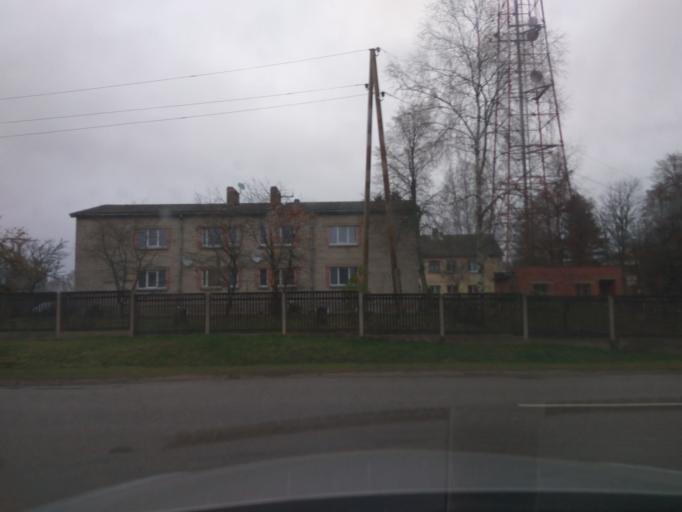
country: LV
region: Kuldigas Rajons
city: Kuldiga
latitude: 56.9344
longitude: 22.0106
